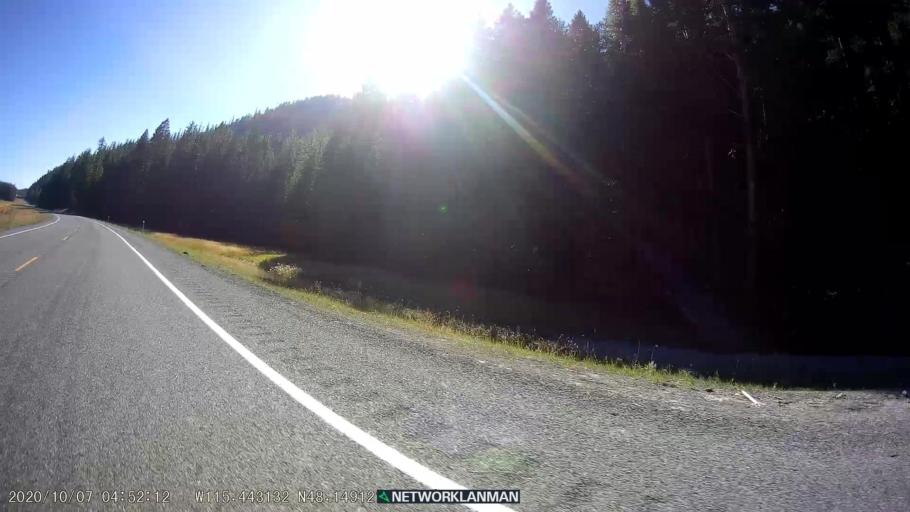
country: US
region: Montana
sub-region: Lincoln County
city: Libby
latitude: 48.1489
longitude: -115.4432
